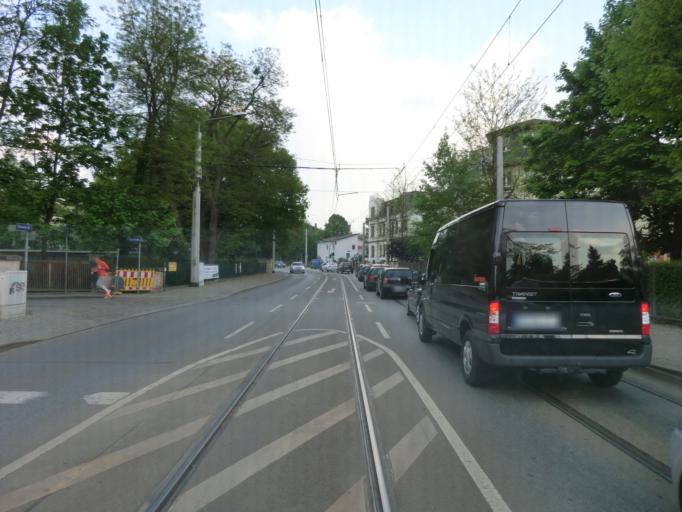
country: DE
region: Saxony
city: Albertstadt
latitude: 51.0490
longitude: 13.8098
